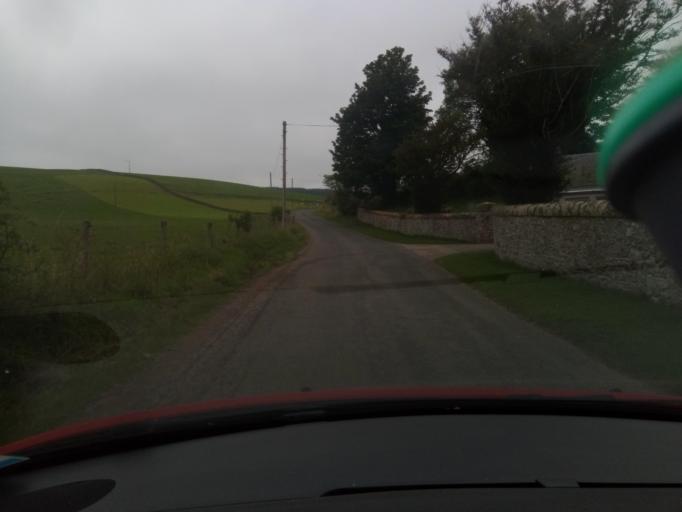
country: GB
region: Scotland
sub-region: The Scottish Borders
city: Galashiels
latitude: 55.7167
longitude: -2.8952
